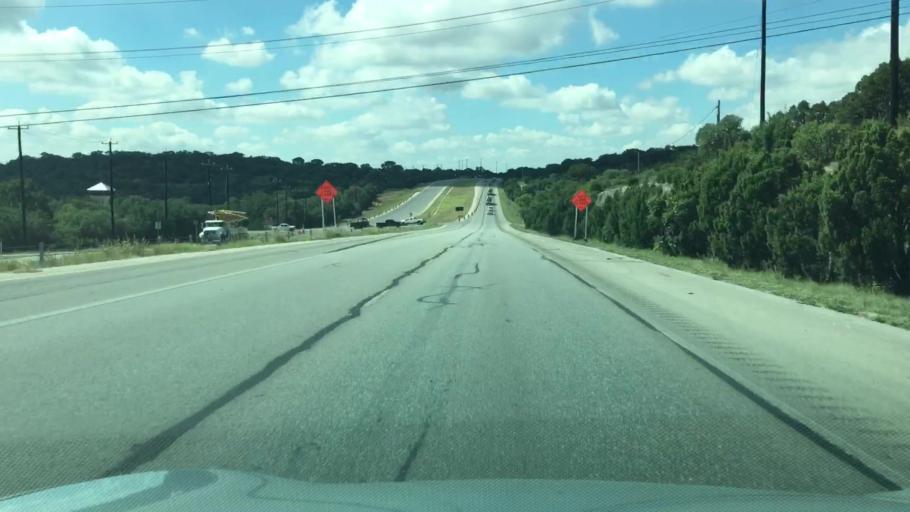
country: US
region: Texas
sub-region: Comal County
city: Bulverde
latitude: 29.7731
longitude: -98.4261
